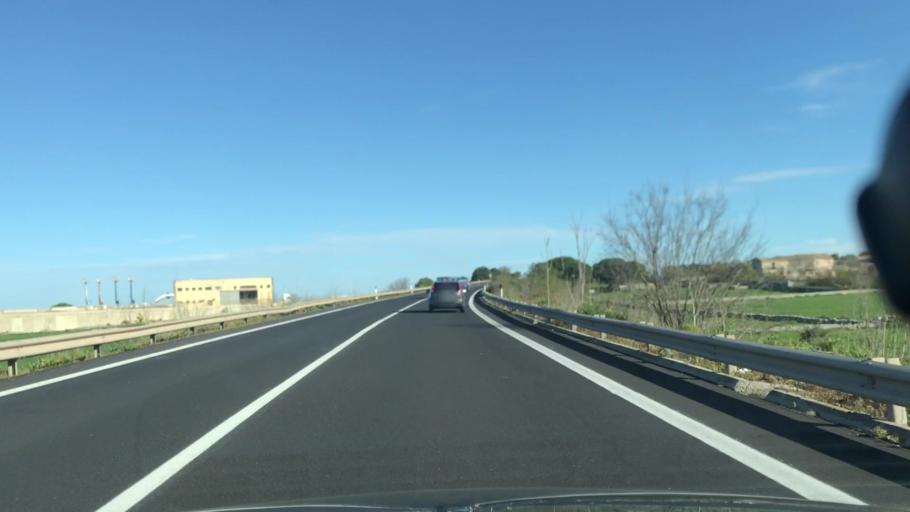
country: IT
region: Sicily
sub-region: Ragusa
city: Comiso
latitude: 36.9351
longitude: 14.6520
